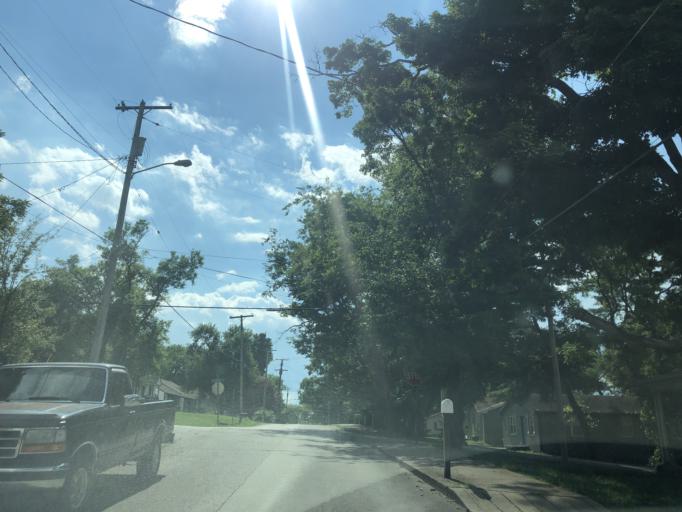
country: US
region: Tennessee
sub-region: Davidson County
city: Nashville
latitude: 36.2081
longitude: -86.7627
